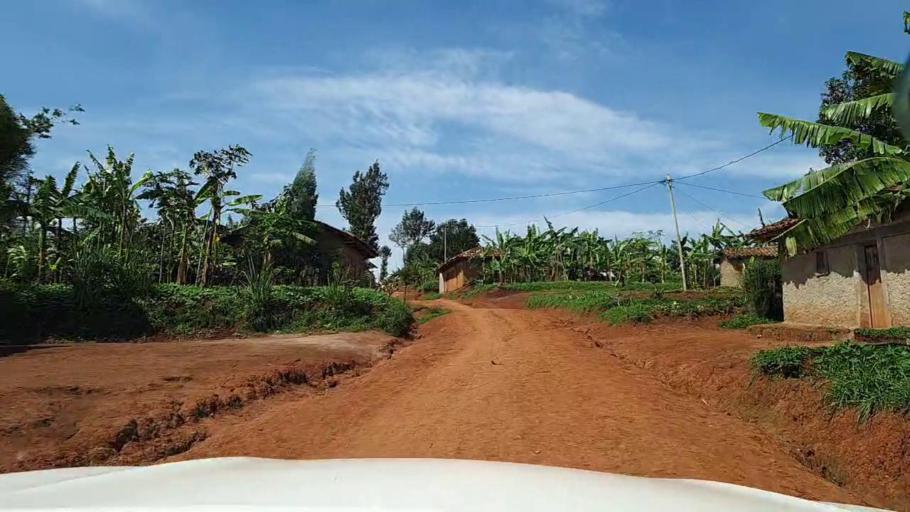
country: RW
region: Southern Province
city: Butare
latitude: -2.7008
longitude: 29.8502
